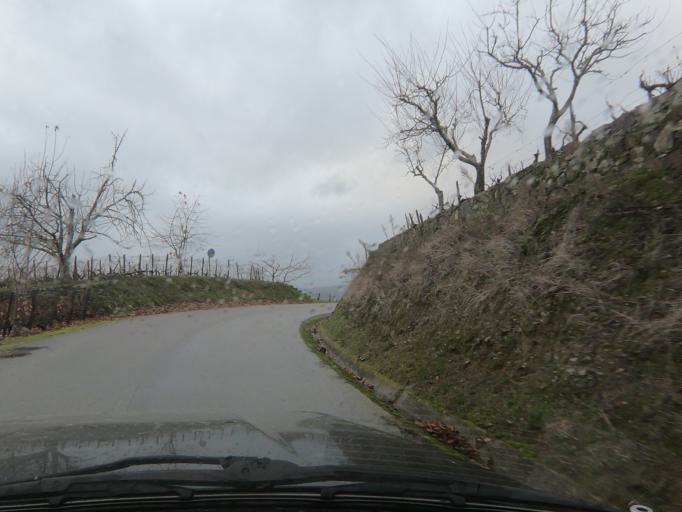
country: PT
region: Vila Real
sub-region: Santa Marta de Penaguiao
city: Santa Marta de Penaguiao
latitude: 41.2037
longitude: -7.7549
